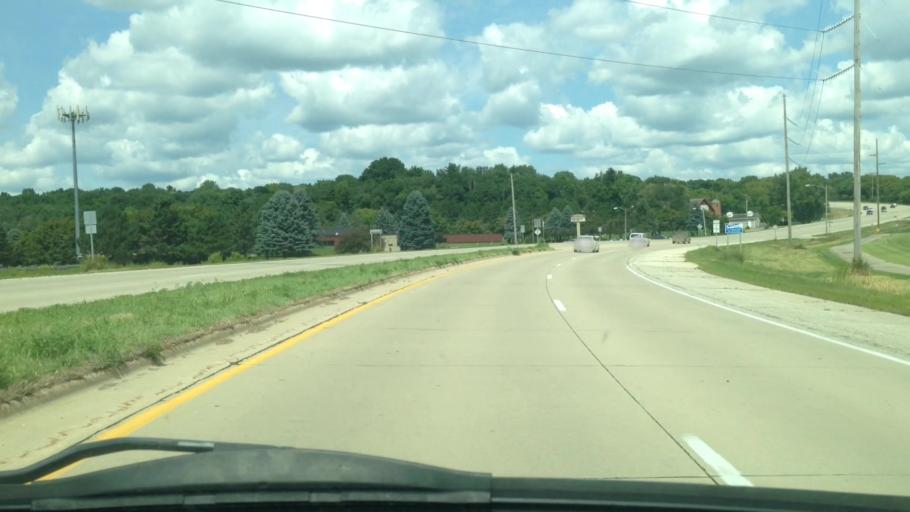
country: US
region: Minnesota
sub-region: Olmsted County
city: Rochester
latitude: 44.0046
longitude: -92.5081
